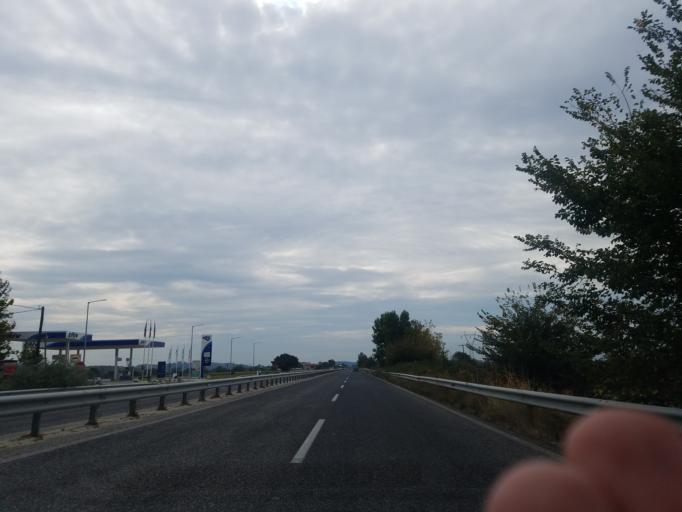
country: GR
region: Thessaly
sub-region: Trikala
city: Vasiliki
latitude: 39.6182
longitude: 21.7149
